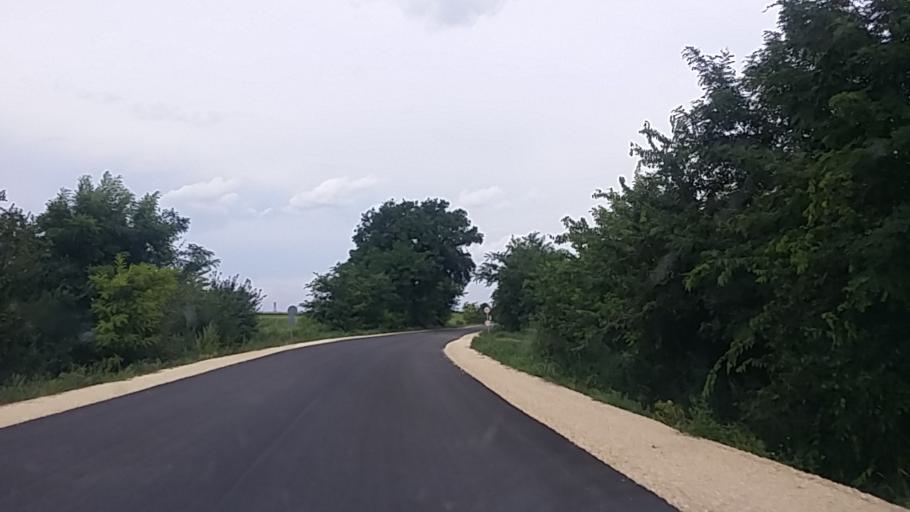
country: HU
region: Tolna
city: Tengelic
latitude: 46.5387
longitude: 18.6658
